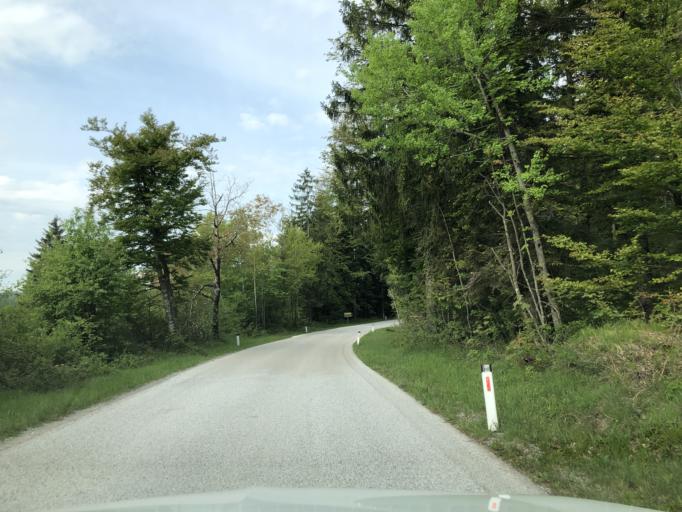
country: SI
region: Bloke
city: Nova Vas
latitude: 45.7954
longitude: 14.5285
